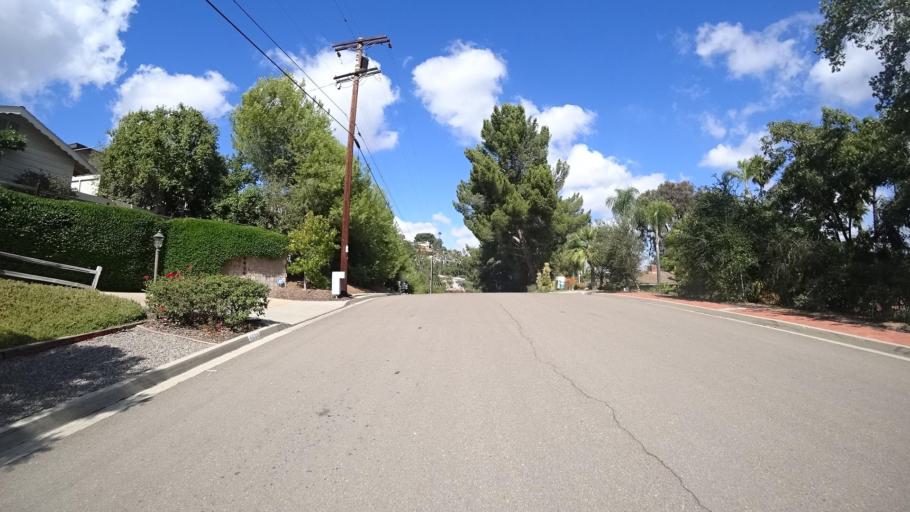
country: US
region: California
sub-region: San Diego County
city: Rancho San Diego
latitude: 32.7640
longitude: -116.9458
